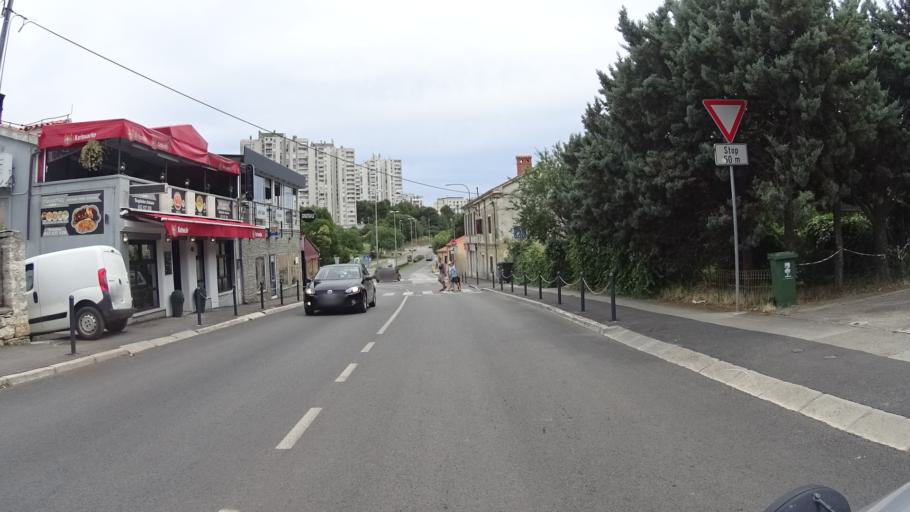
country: HR
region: Istarska
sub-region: Grad Pula
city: Pula
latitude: 44.8550
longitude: 13.8375
